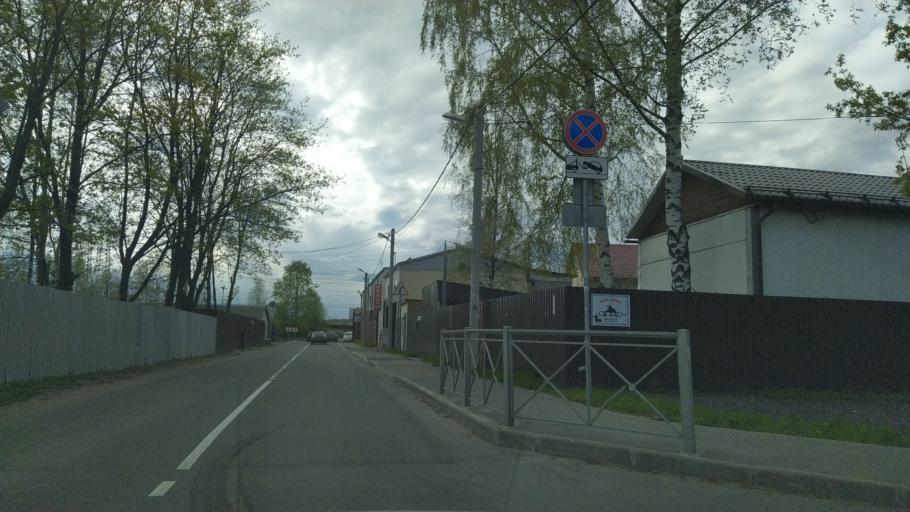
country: RU
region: Leningrad
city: Murino
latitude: 60.0450
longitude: 30.4420
